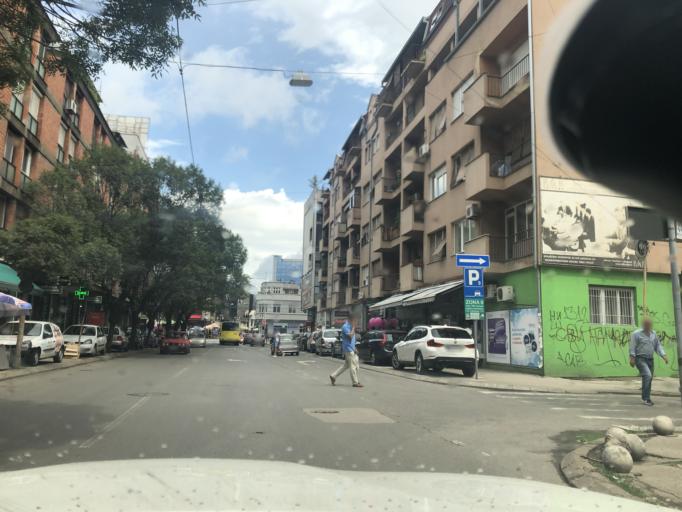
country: RS
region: Central Serbia
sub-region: Nisavski Okrug
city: Nis
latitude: 43.3159
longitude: 21.8946
